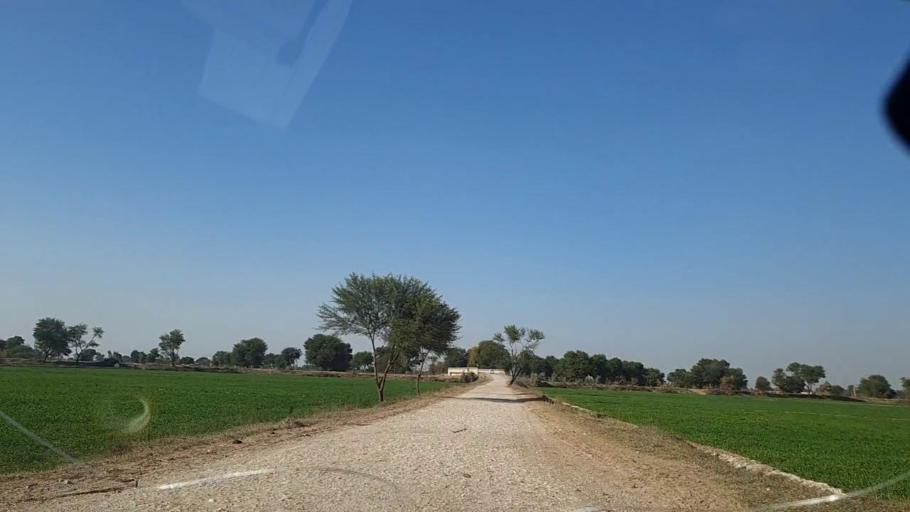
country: PK
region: Sindh
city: Khanpur
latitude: 27.7882
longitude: 69.3517
